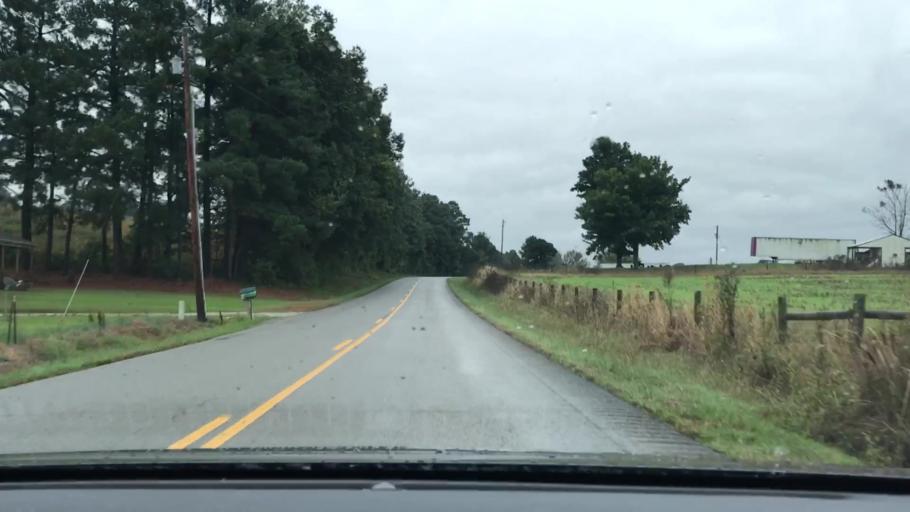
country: US
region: Kentucky
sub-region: McLean County
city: Calhoun
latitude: 37.4815
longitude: -87.2465
